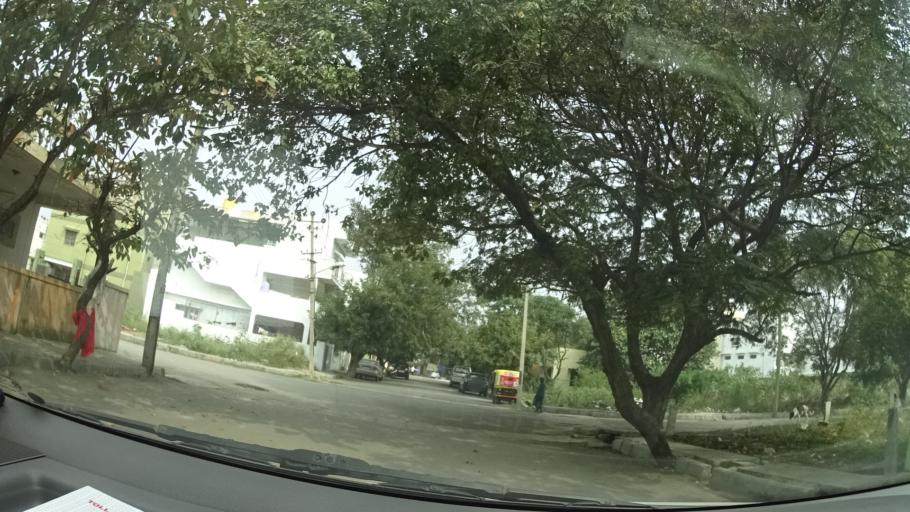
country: IN
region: Karnataka
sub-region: Bangalore Urban
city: Bangalore
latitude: 13.0279
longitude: 77.6245
